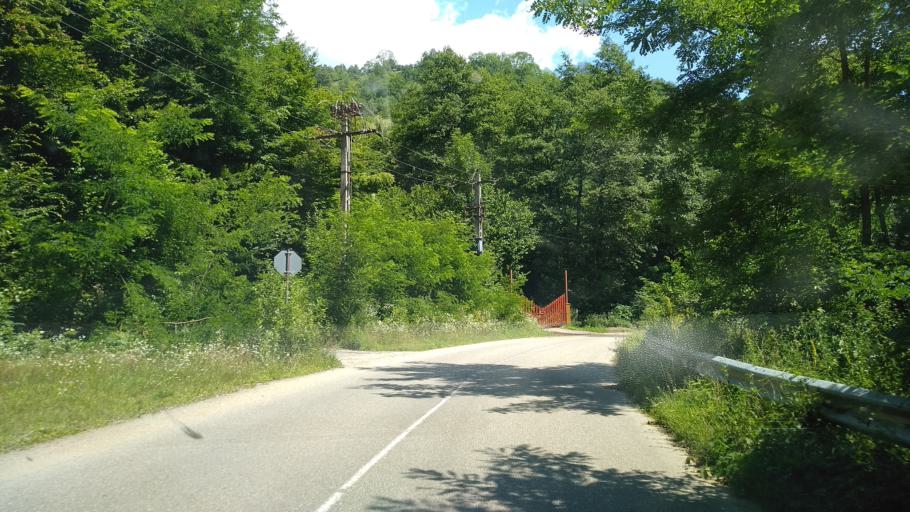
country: RO
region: Hunedoara
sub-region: Comuna Orastioara de Sus
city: Orastioara de Sus
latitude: 45.6611
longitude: 23.1786
